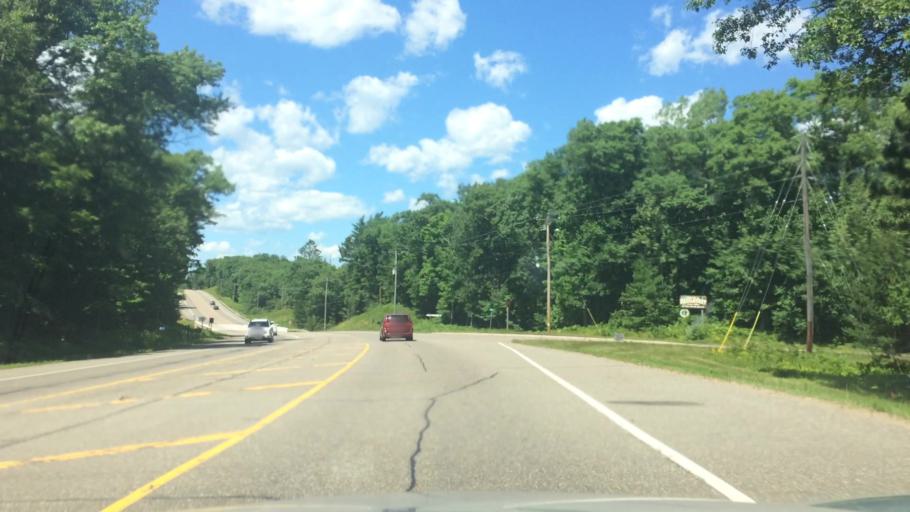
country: US
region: Wisconsin
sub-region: Vilas County
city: Lac du Flambeau
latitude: 45.7897
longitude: -89.7105
